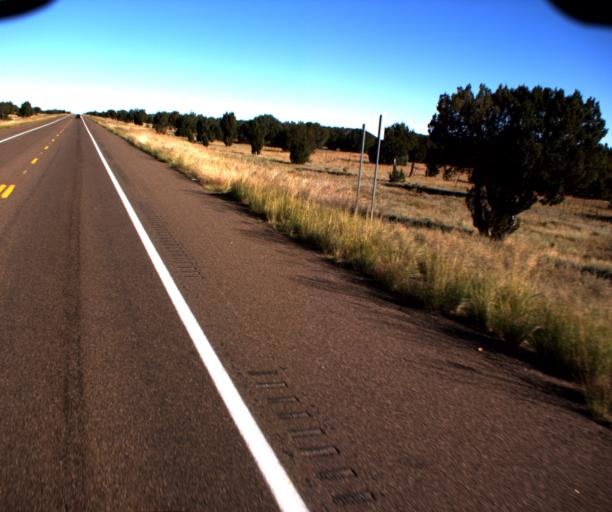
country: US
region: Arizona
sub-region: Navajo County
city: Show Low
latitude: 34.2754
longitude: -110.0252
